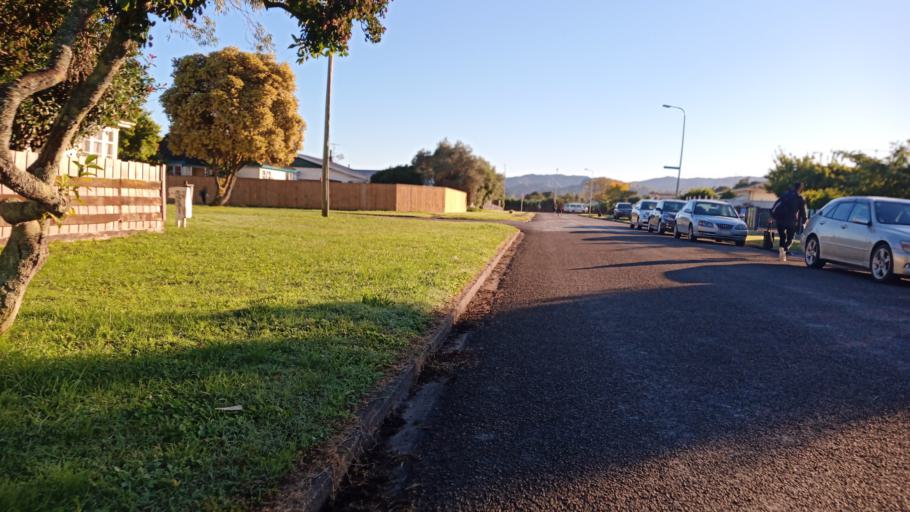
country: NZ
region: Gisborne
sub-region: Gisborne District
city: Gisborne
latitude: -38.6598
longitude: 178.0015
